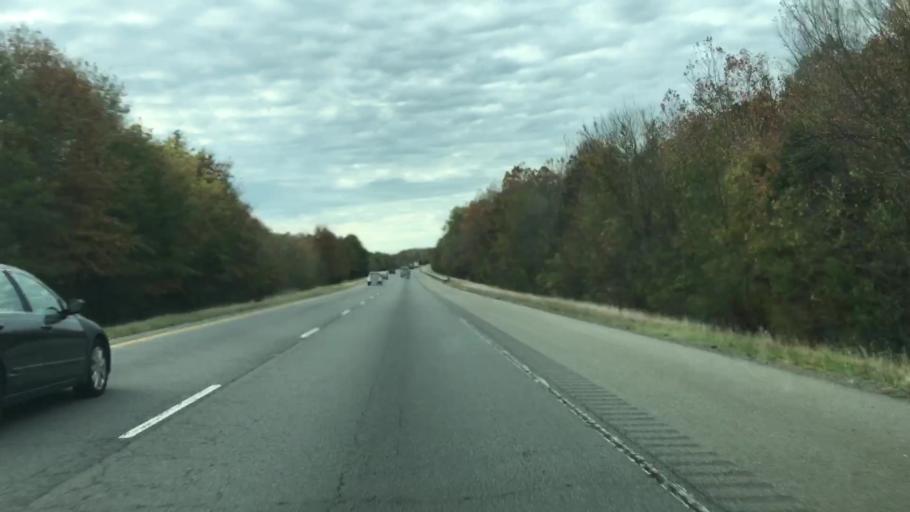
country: US
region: Arkansas
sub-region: Faulkner County
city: Conway
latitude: 35.1206
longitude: -92.4812
